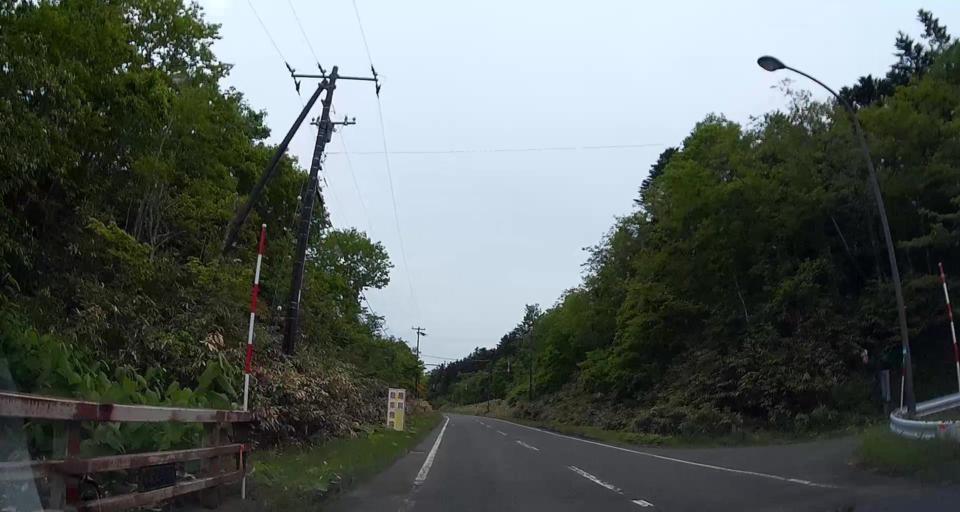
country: JP
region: Hokkaido
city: Shiraoi
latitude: 42.6363
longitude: 141.2388
